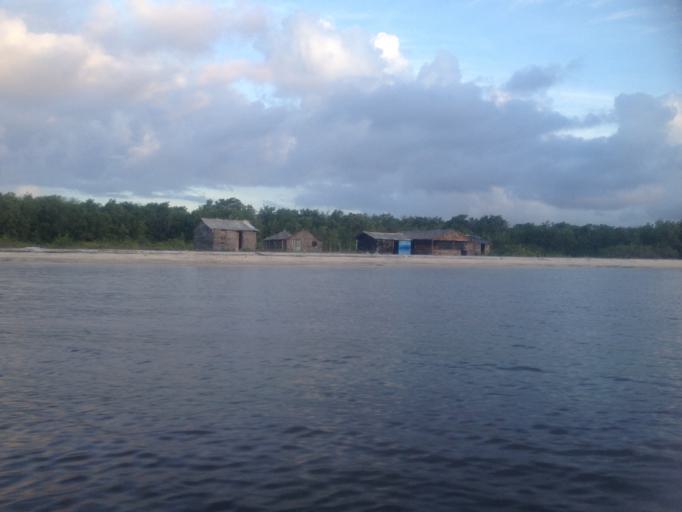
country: BR
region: Sergipe
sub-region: Indiaroba
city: Indiaroba
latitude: -11.4755
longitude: -37.3833
